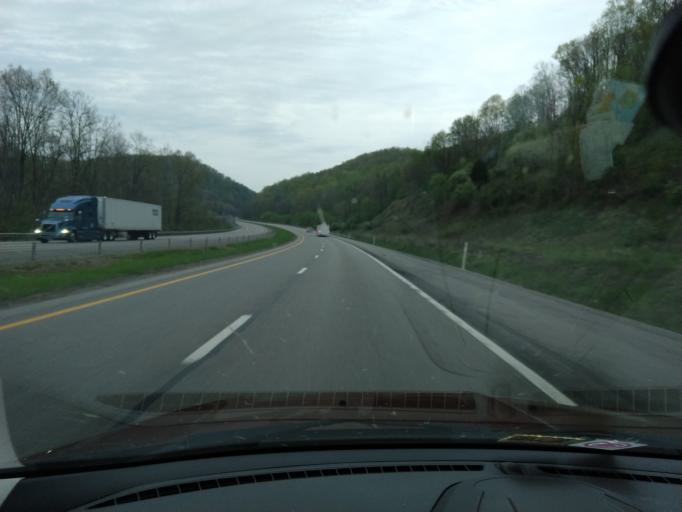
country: US
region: West Virginia
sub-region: Lewis County
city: Weston
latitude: 38.9710
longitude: -80.5119
